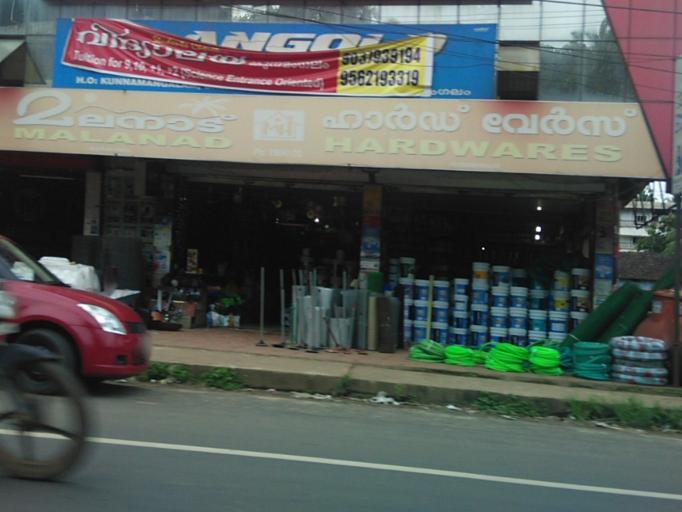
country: IN
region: Kerala
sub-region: Kozhikode
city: Kunnamangalam
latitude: 11.3043
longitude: 75.8768
